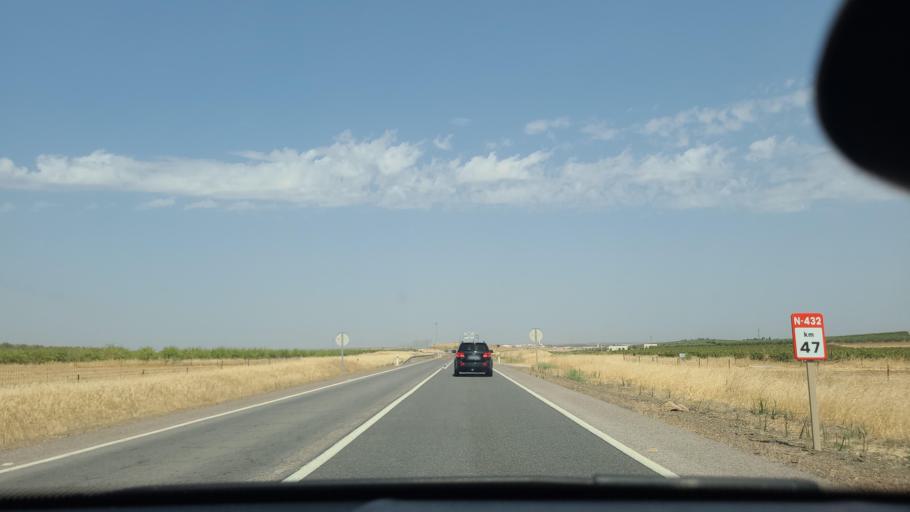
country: ES
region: Extremadura
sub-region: Provincia de Badajoz
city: Santa Marta
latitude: 38.5867
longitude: -6.6018
